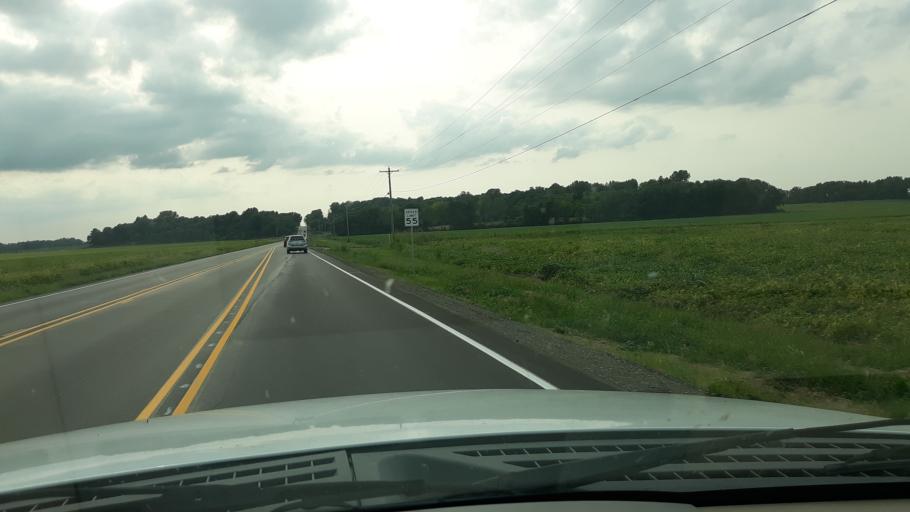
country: US
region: Indiana
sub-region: Gibson County
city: Princeton
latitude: 38.3558
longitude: -87.6447
